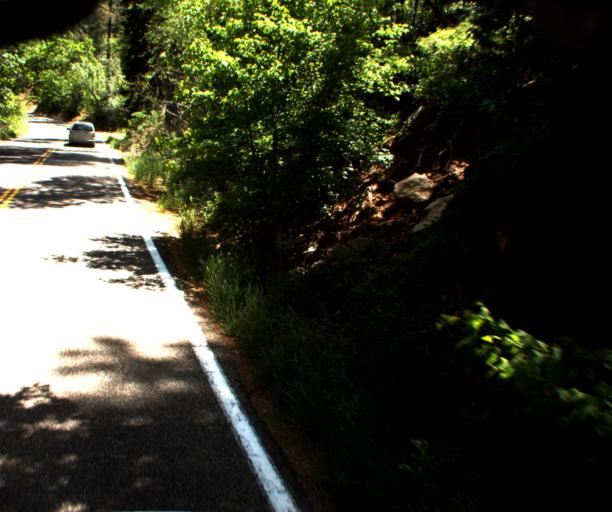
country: US
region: Arizona
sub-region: Coconino County
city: Sedona
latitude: 34.9372
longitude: -111.7476
